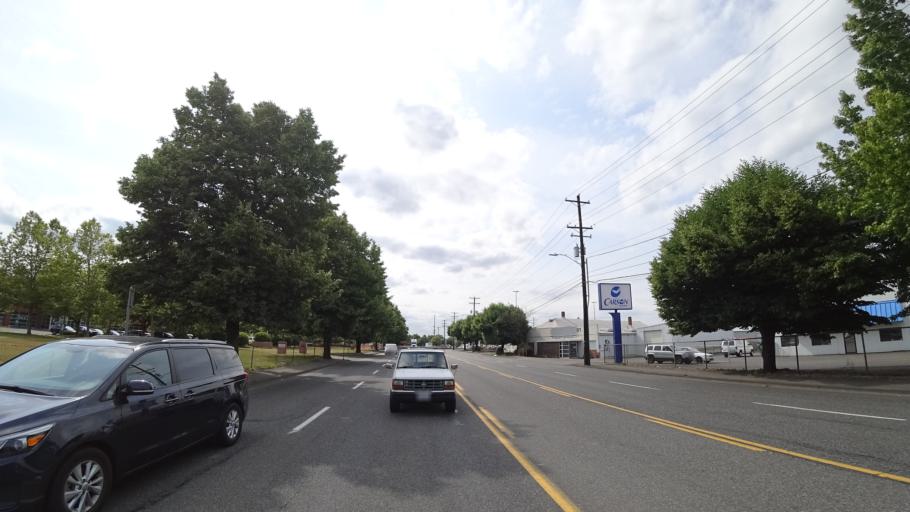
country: US
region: Washington
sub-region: Clark County
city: Vancouver
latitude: 45.5821
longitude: -122.6648
